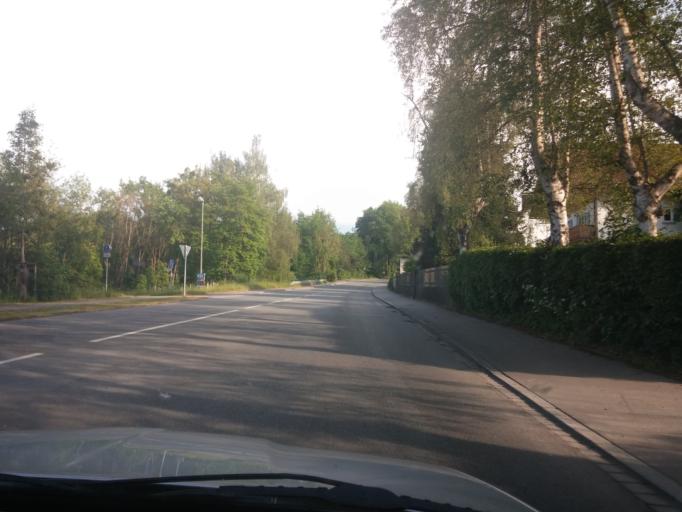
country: DE
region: Bavaria
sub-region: Swabia
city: Lautrach
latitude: 47.9012
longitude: 10.1193
